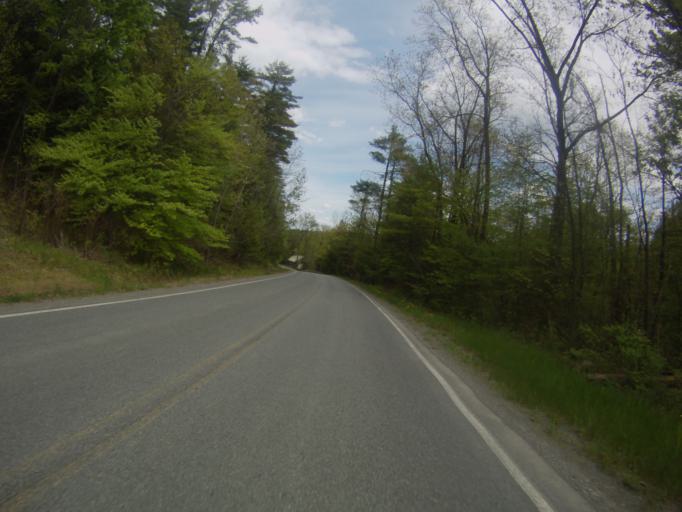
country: US
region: New York
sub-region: Essex County
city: Ticonderoga
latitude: 43.9416
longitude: -73.4730
